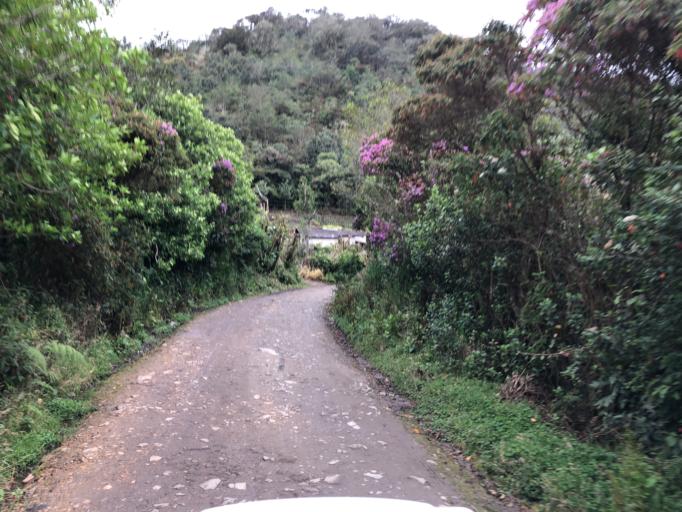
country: CO
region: Cauca
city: Totoro
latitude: 2.4974
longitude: -76.3476
